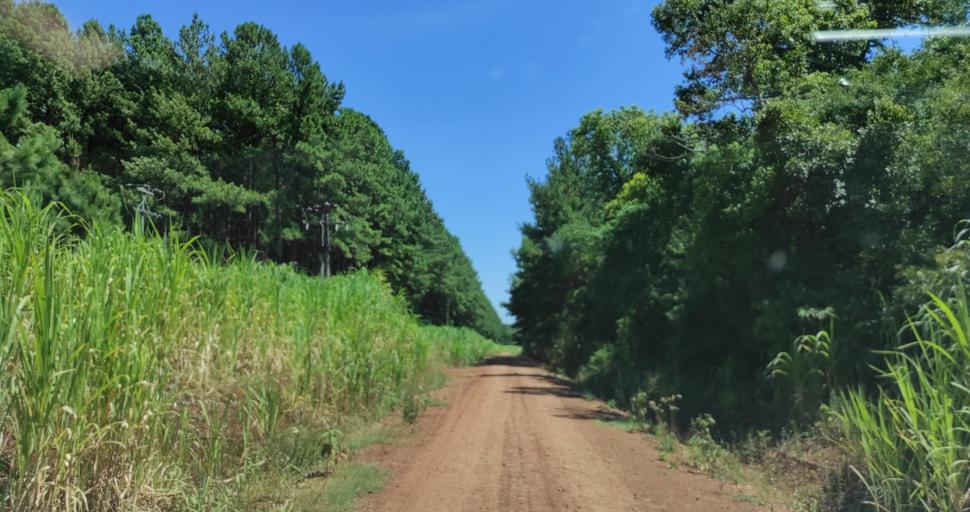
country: AR
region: Misiones
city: Capiovi
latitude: -26.9274
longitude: -55.0969
